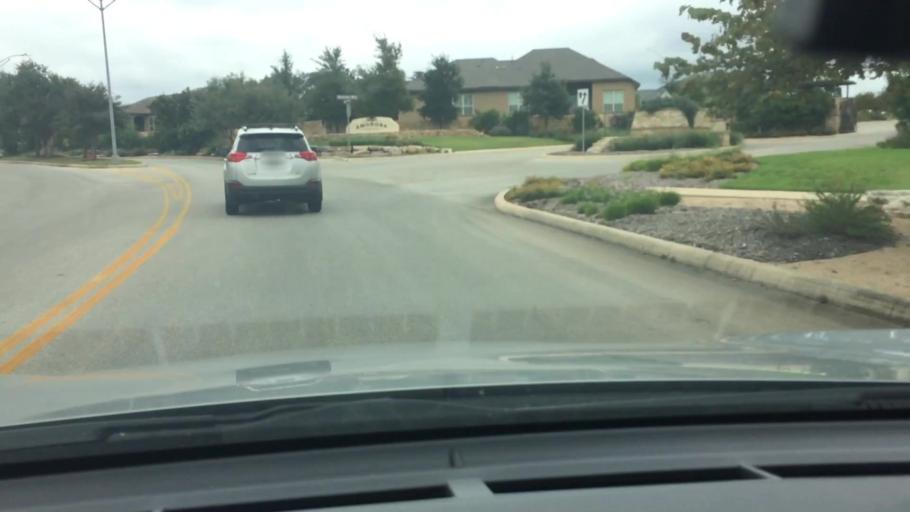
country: US
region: Texas
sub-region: Bexar County
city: Timberwood Park
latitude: 29.6566
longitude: -98.4010
